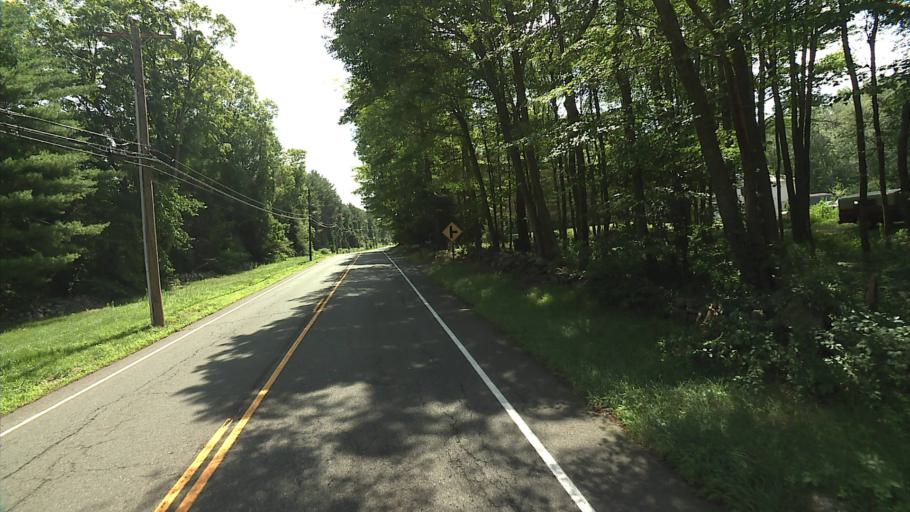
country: US
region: Connecticut
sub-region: Tolland County
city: Coventry Lake
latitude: 41.7899
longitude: -72.3478
